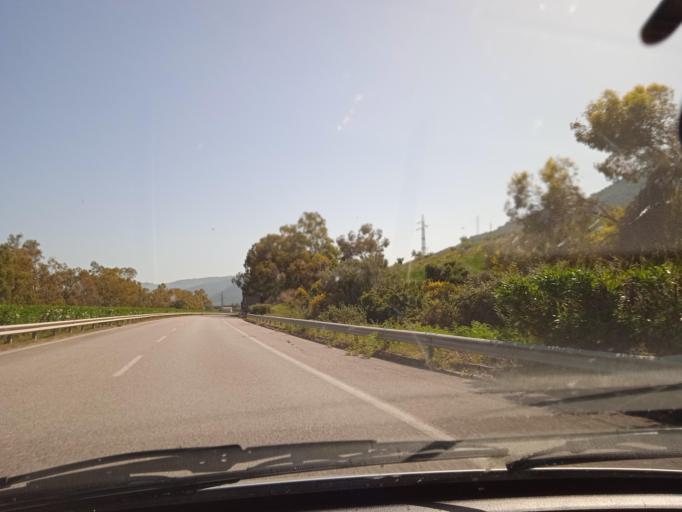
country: IT
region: Sicily
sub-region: Messina
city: Torrenova
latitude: 38.0917
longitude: 14.6967
